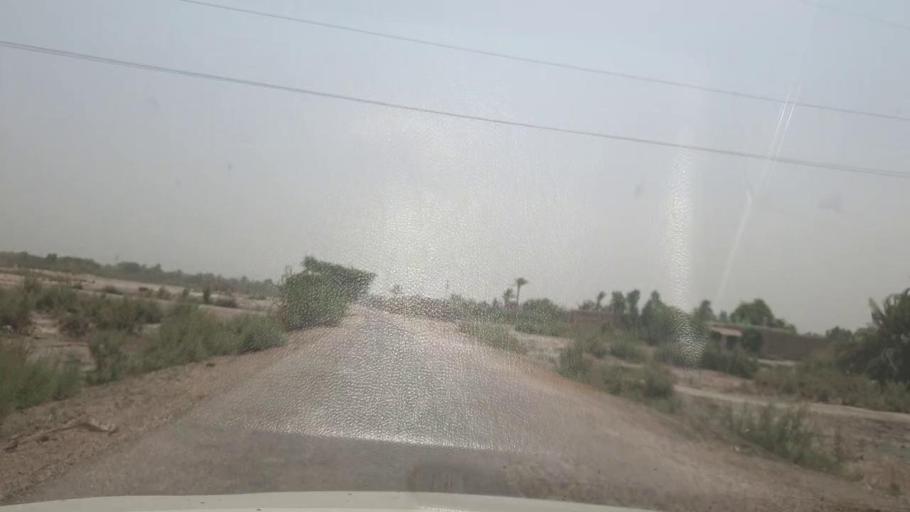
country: PK
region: Sindh
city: Kot Diji
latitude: 27.3759
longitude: 68.7024
